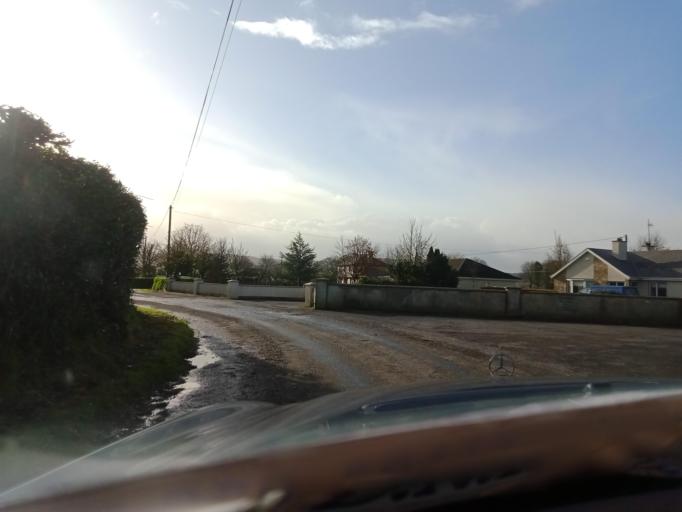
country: IE
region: Leinster
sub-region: Kilkenny
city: Mooncoin
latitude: 52.2897
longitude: -7.2733
